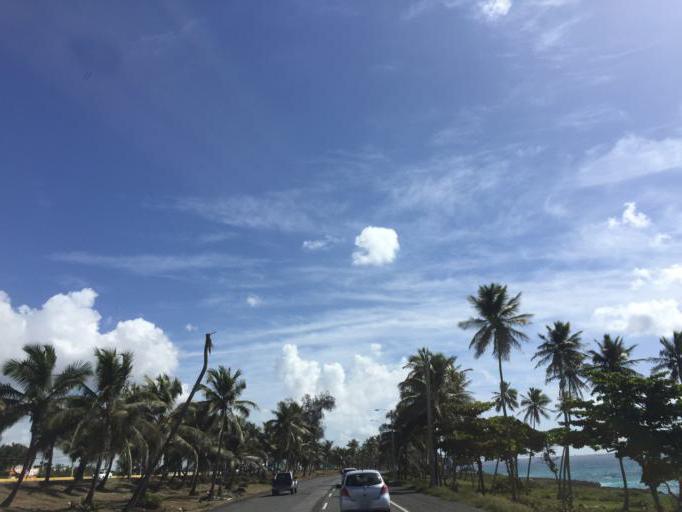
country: DO
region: Santo Domingo
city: Guerra
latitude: 18.4610
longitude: -69.7323
